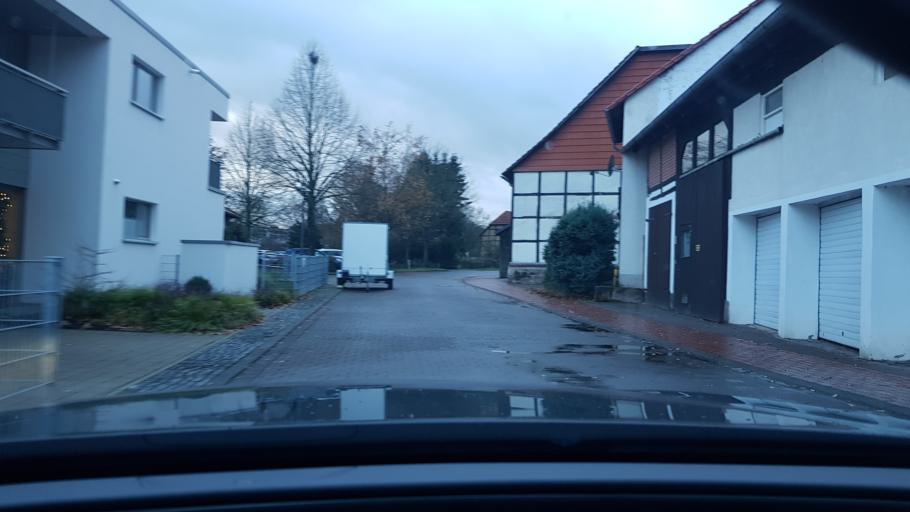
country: DE
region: Lower Saxony
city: Hardegsen
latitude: 51.6504
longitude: 9.8308
